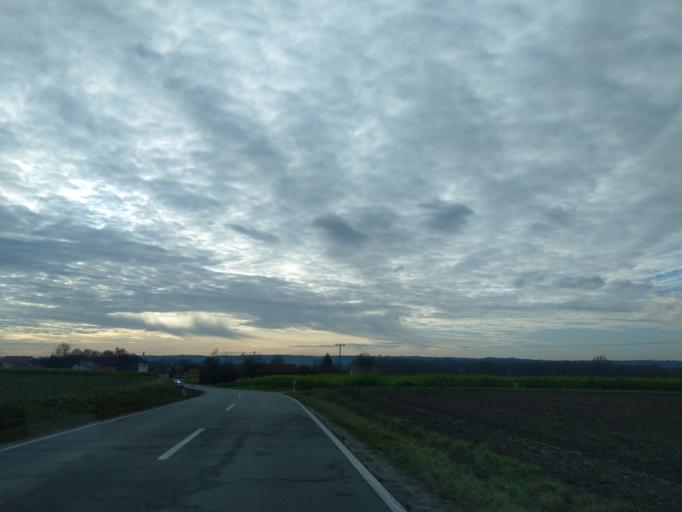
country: DE
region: Bavaria
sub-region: Lower Bavaria
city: Buchhofen
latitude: 48.7018
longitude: 12.9417
